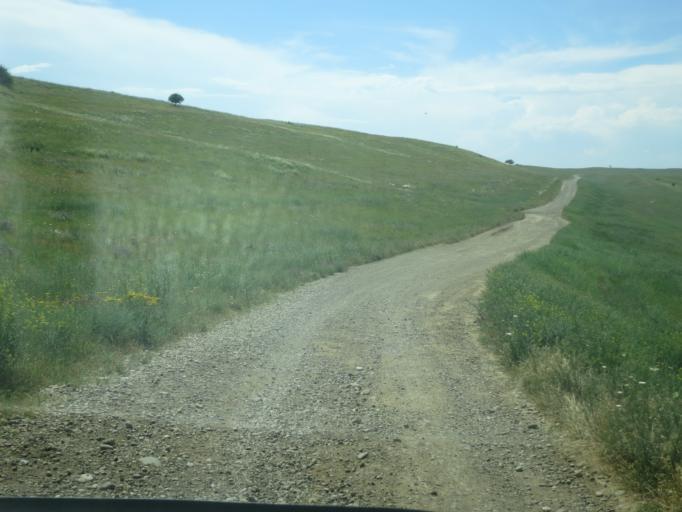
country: AZ
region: Agstafa
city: Saloglu
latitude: 41.4671
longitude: 45.3298
